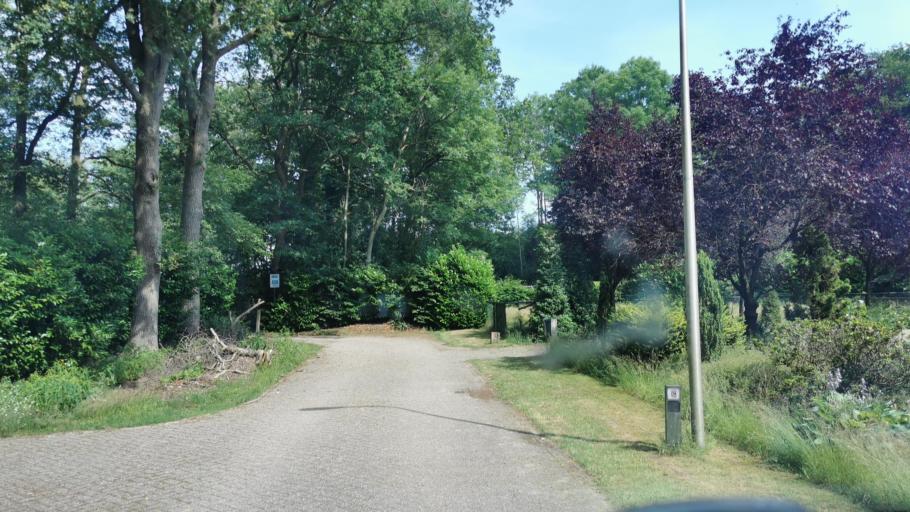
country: NL
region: Overijssel
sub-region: Gemeente Oldenzaal
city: Oldenzaal
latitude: 52.3038
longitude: 6.8812
